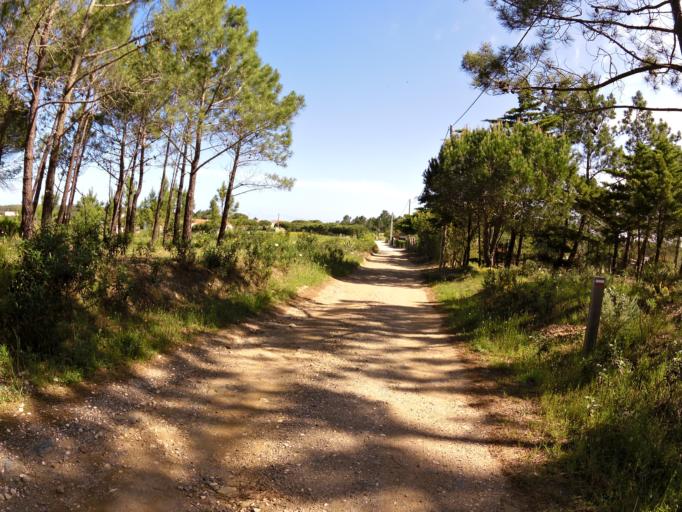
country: PT
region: Faro
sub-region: Aljezur
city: Aljezur
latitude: 37.3346
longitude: -8.8088
